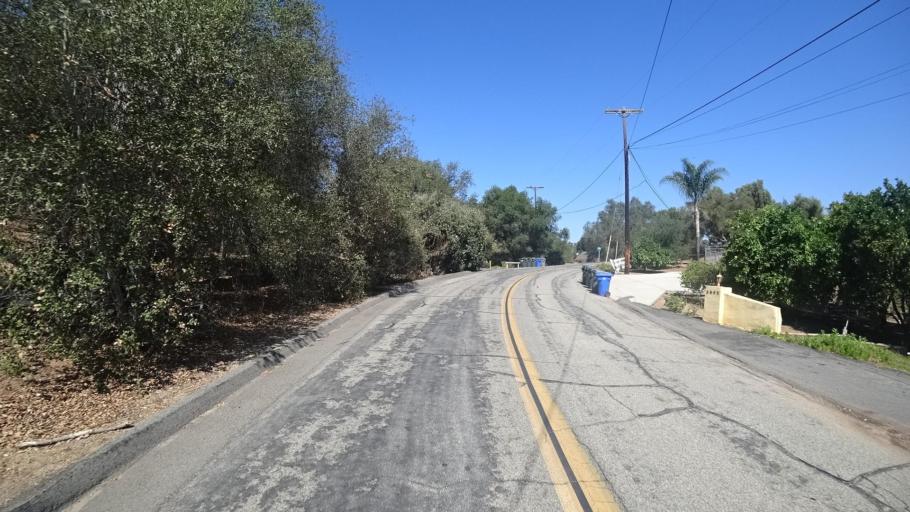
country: US
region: California
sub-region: San Diego County
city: Bonsall
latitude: 33.3190
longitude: -117.2271
